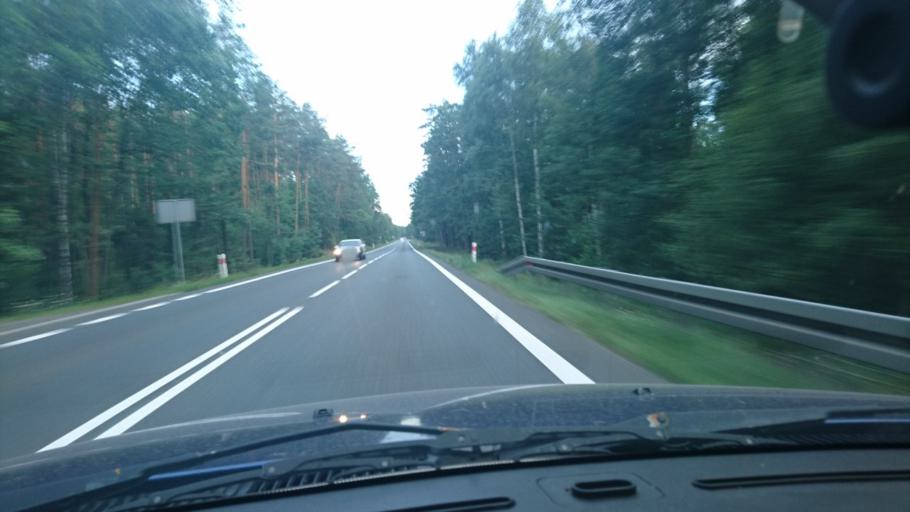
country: PL
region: Silesian Voivodeship
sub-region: Powiat lubliniecki
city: Lubliniec
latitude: 50.6101
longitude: 18.6945
